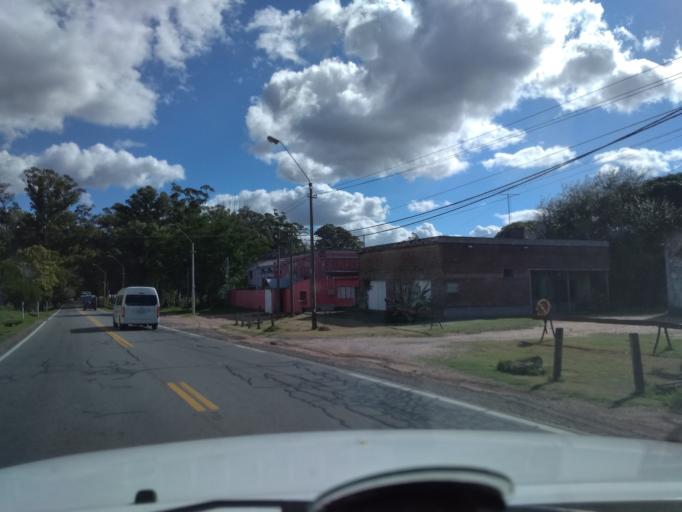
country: UY
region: Canelones
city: Canelones
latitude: -34.5192
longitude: -56.2631
